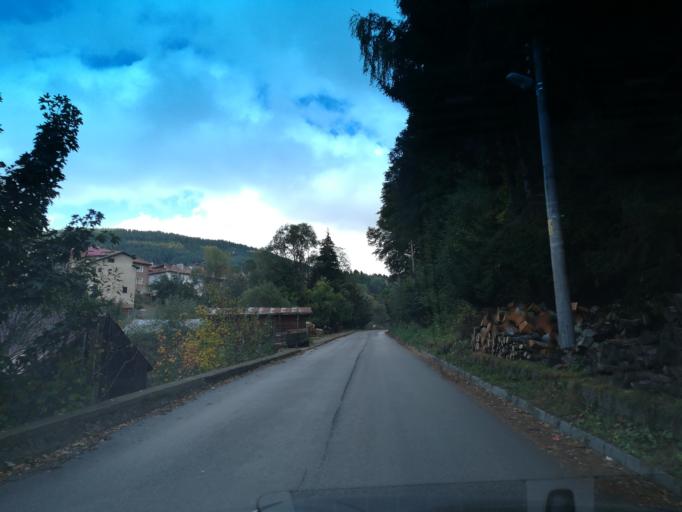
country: BG
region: Pazardzhik
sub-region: Obshtina Batak
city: Batak
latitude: 41.9358
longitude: 24.2699
